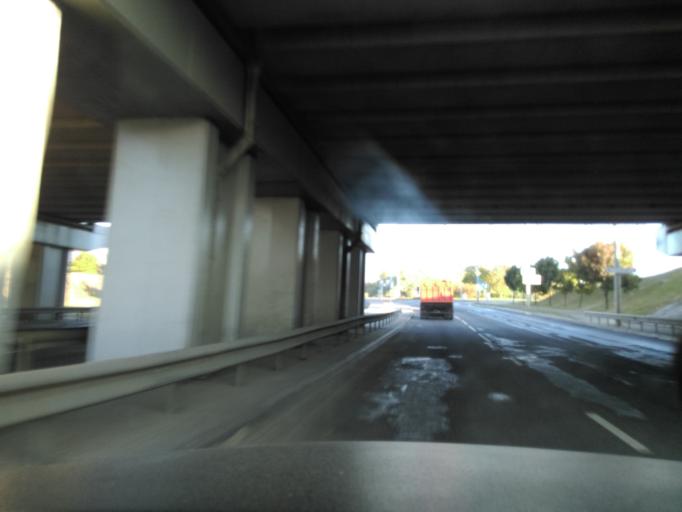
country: BY
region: Minsk
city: Minsk
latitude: 53.8881
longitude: 27.5798
